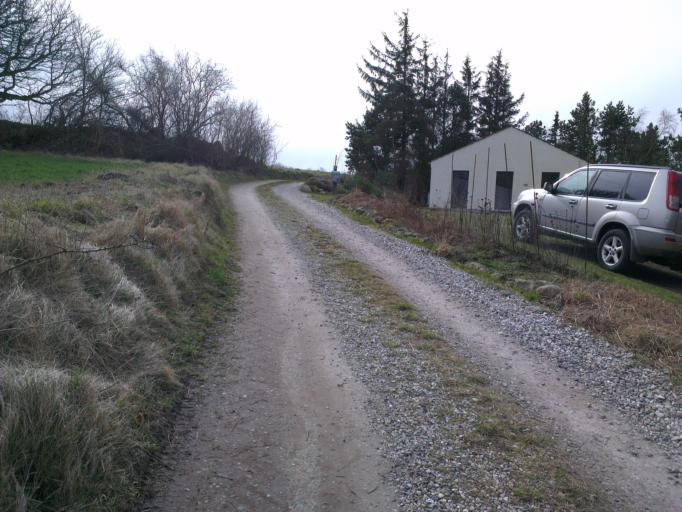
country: DK
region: Zealand
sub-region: Lejre Kommune
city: Ejby
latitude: 55.7838
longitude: 11.8649
